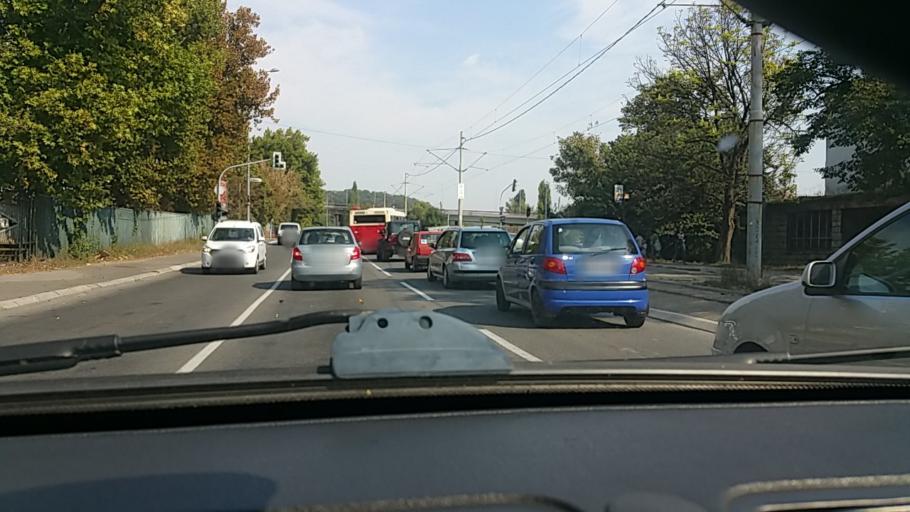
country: RS
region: Central Serbia
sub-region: Belgrade
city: Rakovica
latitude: 44.7424
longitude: 20.4410
